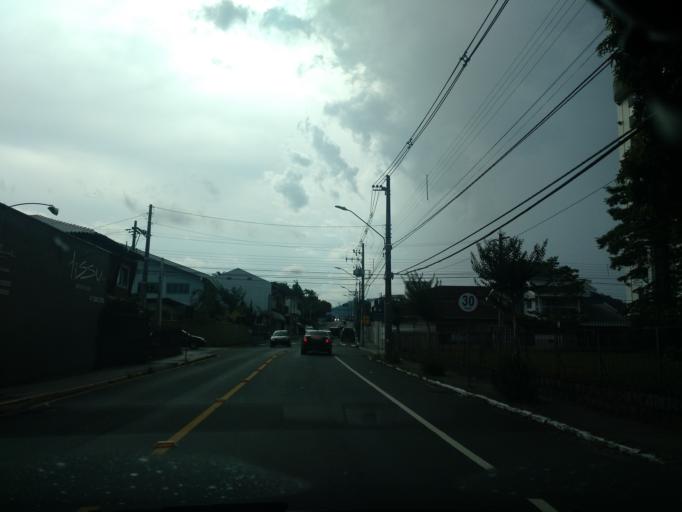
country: BR
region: Santa Catarina
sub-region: Jaragua Do Sul
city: Jaragua do Sul
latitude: -26.4836
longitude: -49.0946
